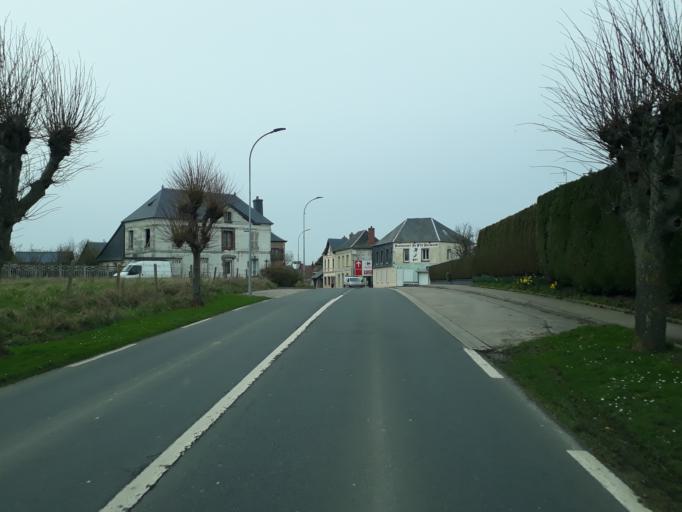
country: FR
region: Haute-Normandie
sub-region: Departement de la Seine-Maritime
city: Breaute
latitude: 49.6259
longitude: 0.3995
